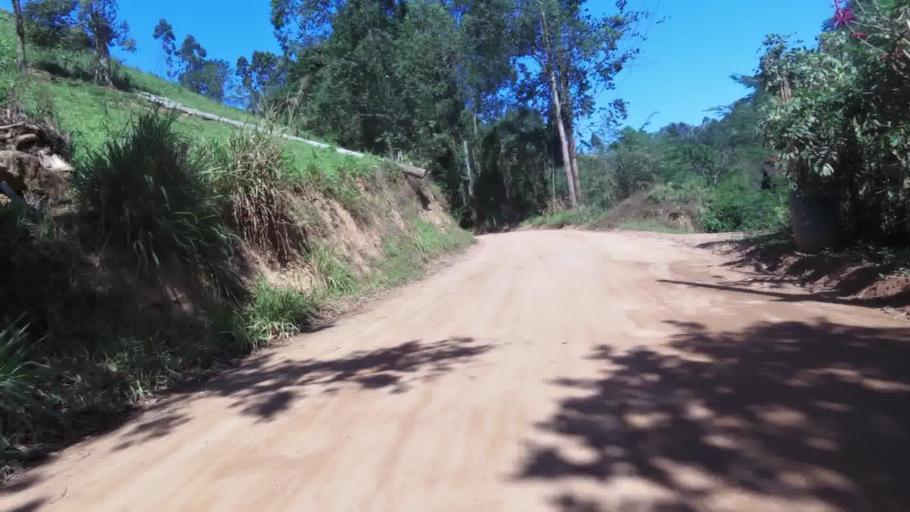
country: BR
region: Espirito Santo
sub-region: Alfredo Chaves
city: Alfredo Chaves
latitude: -20.6505
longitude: -40.8046
